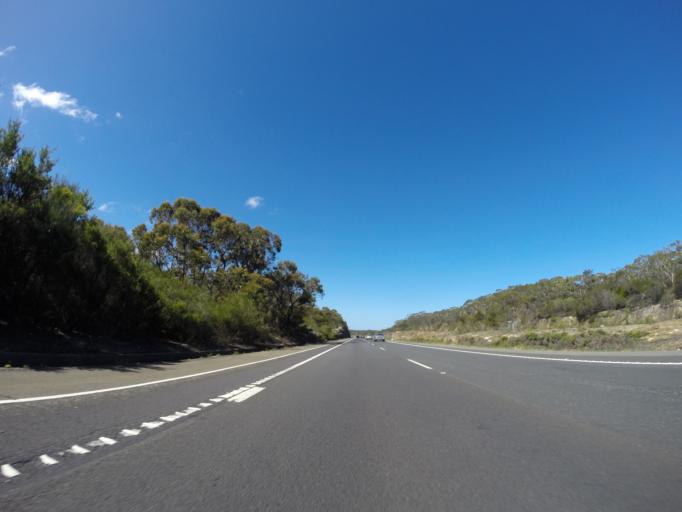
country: AU
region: New South Wales
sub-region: Wollongong
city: Bulli
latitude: -34.2939
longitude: 150.9191
